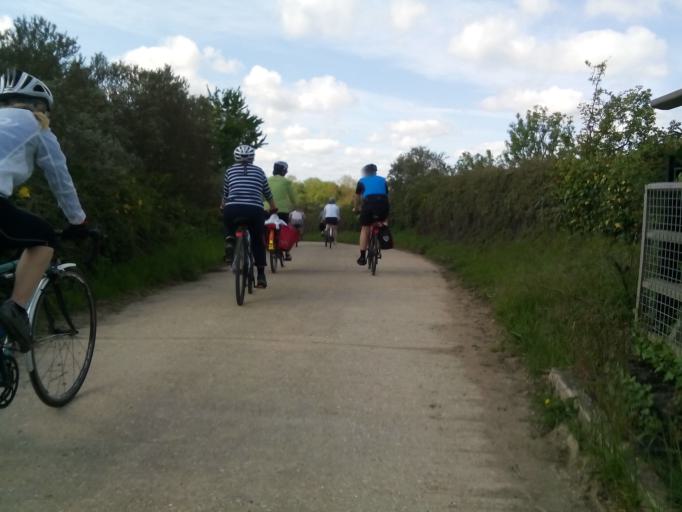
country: GB
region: England
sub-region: Cambridgeshire
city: Grantchester
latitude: 52.1638
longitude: 0.0966
